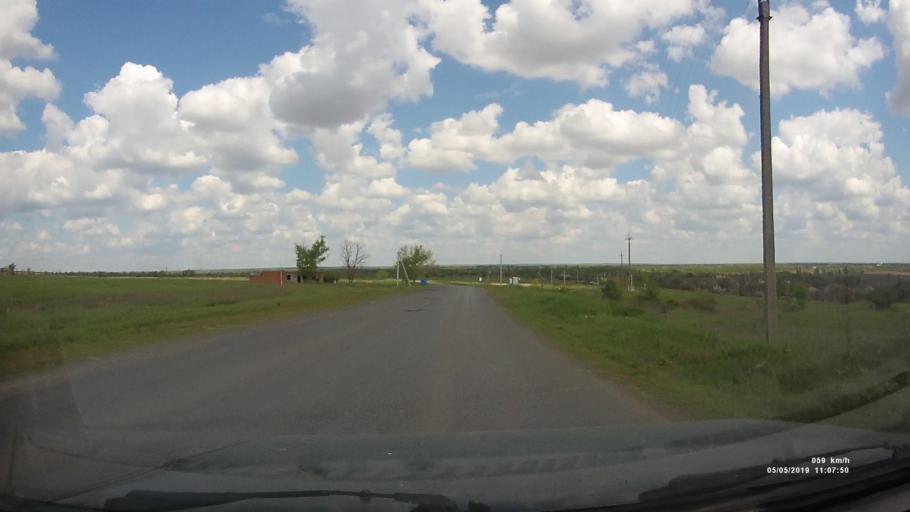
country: RU
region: Rostov
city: Ust'-Donetskiy
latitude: 47.7288
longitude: 40.9141
